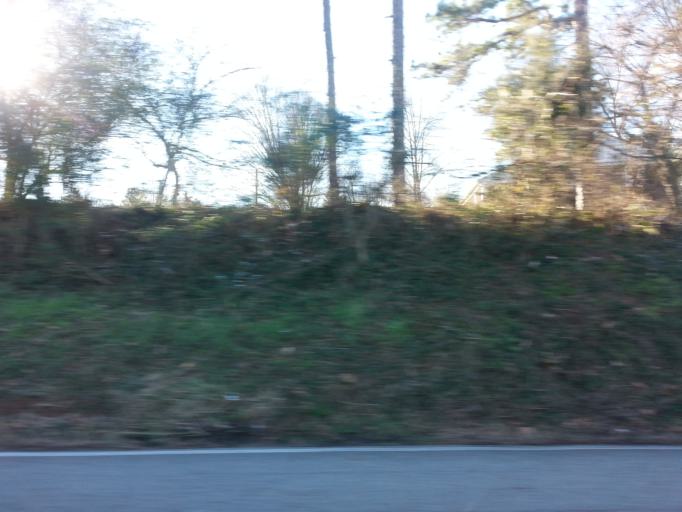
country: US
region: Tennessee
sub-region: Knox County
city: Knoxville
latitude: 35.8956
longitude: -83.9764
